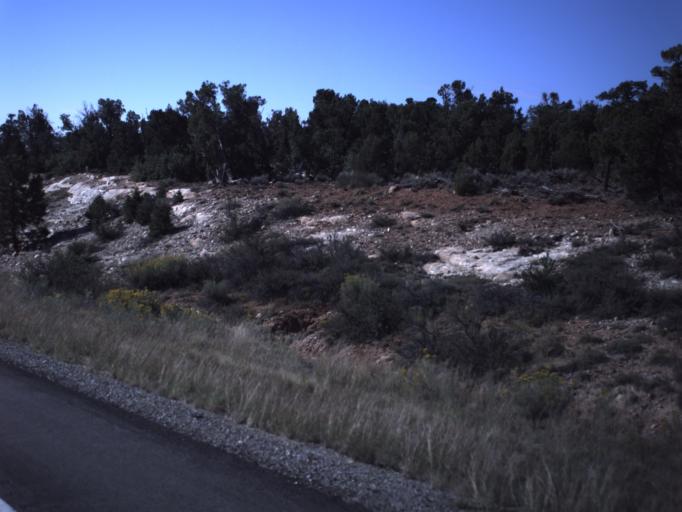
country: US
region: Utah
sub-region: San Juan County
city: Blanding
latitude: 37.6796
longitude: -109.4320
